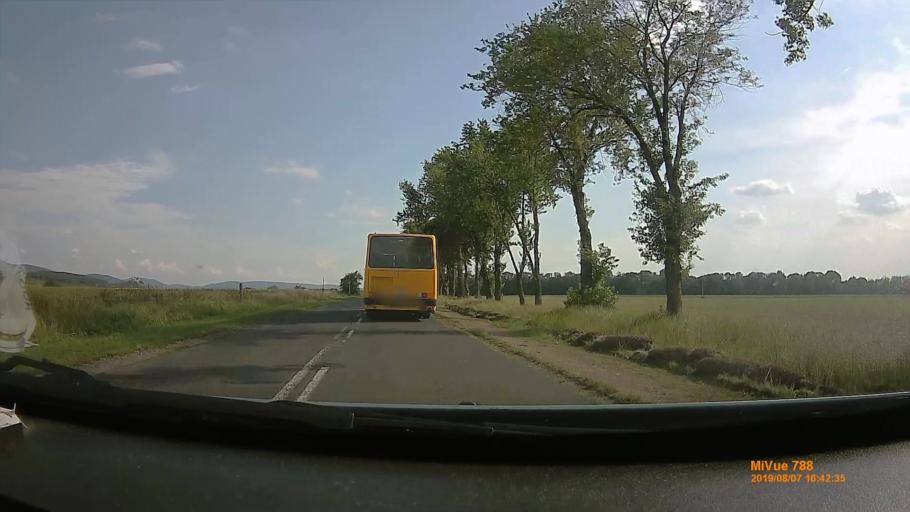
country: HU
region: Borsod-Abauj-Zemplen
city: Abaujszanto
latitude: 48.3679
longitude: 21.2158
